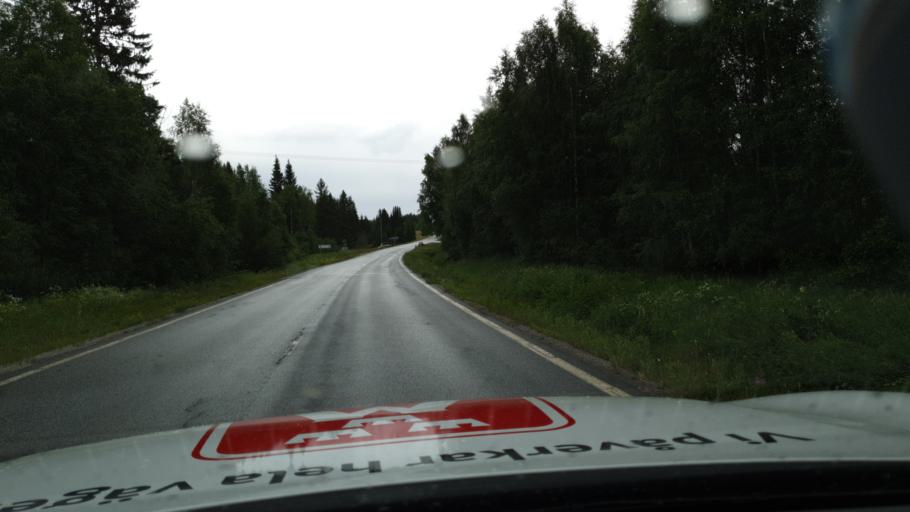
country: SE
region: Vaesterbotten
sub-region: Dorotea Kommun
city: Dorotea
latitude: 63.8287
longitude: 16.4058
